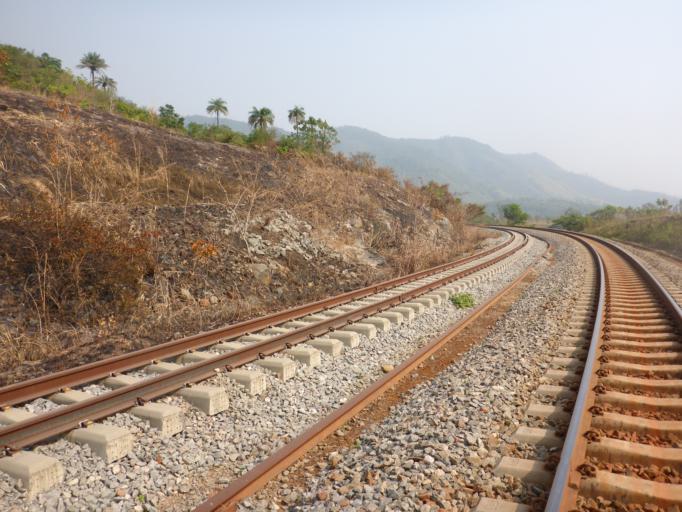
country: SL
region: Northern Province
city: Bumbuna
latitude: 8.9548
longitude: -11.7559
